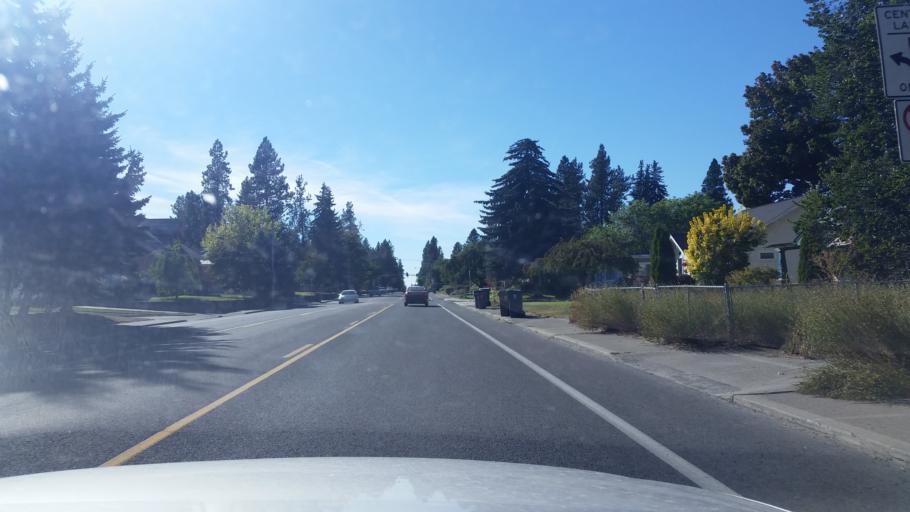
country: US
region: Washington
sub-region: Spokane County
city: Spokane
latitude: 47.6282
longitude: -117.4130
